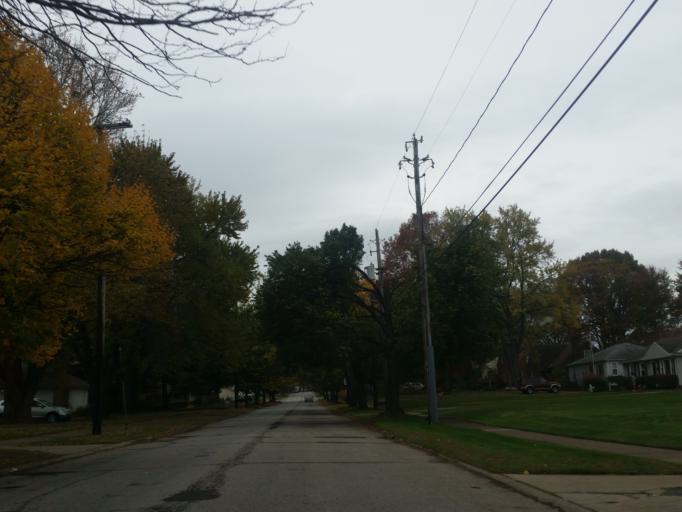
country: US
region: Ohio
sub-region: Cuyahoga County
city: Brooklyn Heights
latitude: 41.4295
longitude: -81.6875
